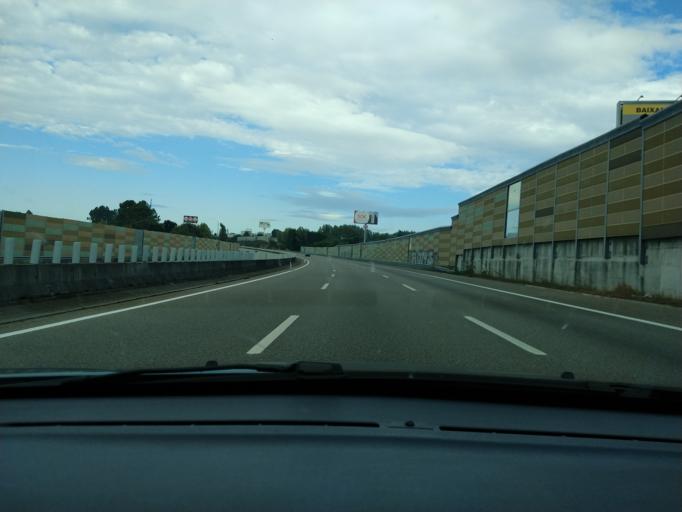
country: PT
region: Aveiro
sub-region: Santa Maria da Feira
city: Pacos de Brandao
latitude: 40.9806
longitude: -8.5770
